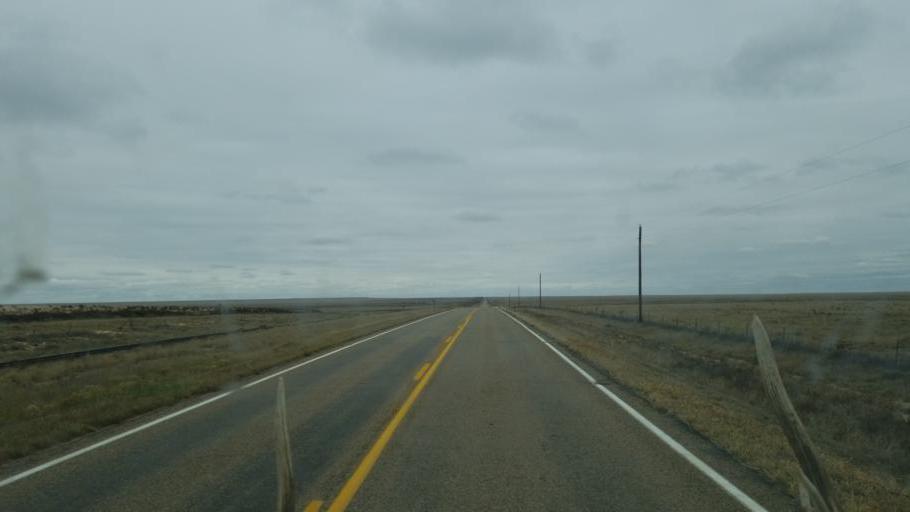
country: US
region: Colorado
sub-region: Crowley County
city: Ordway
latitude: 38.2422
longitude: -103.6215
